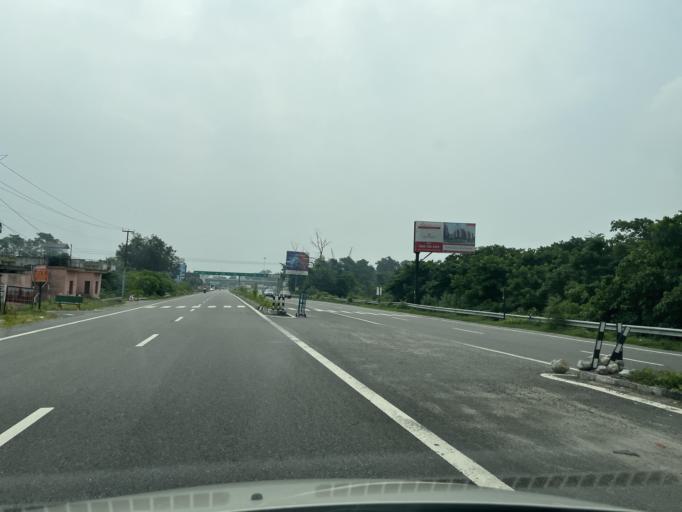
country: IN
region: Uttarakhand
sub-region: Dehradun
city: Raiwala
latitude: 30.0571
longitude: 78.2159
